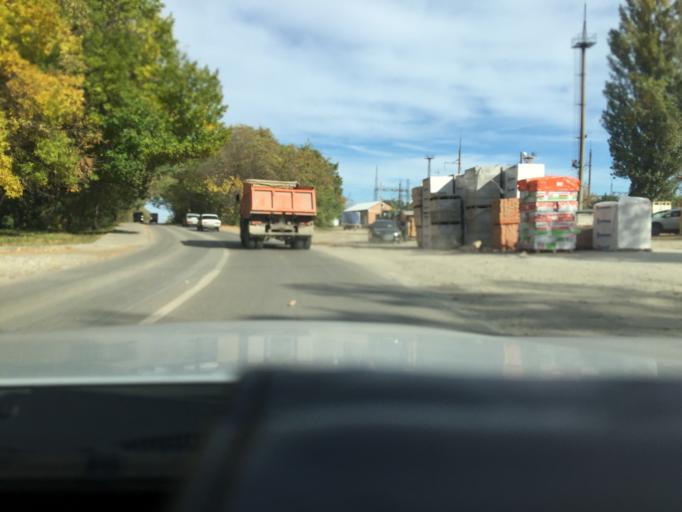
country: RU
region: Rostov
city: Imeni Chkalova
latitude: 47.2897
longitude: 39.8038
